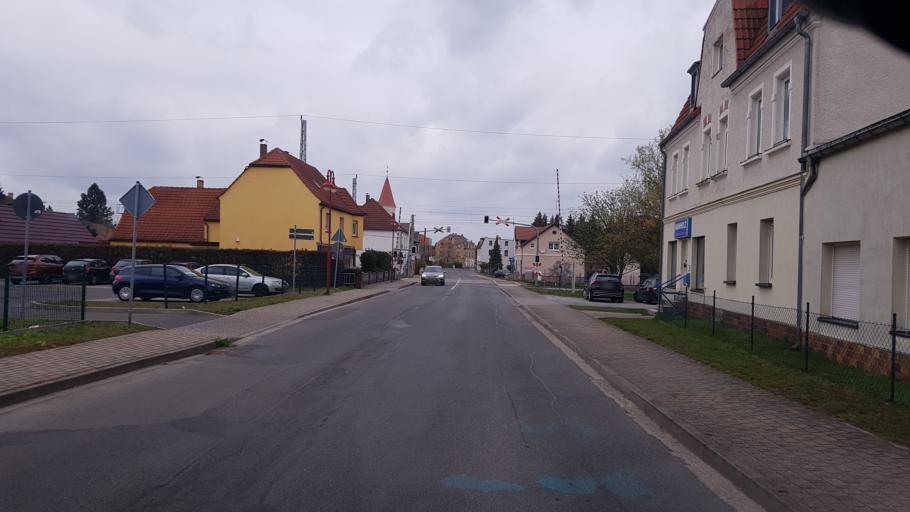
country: DE
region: Brandenburg
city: Hohenbocka
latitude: 51.4531
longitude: 14.0258
